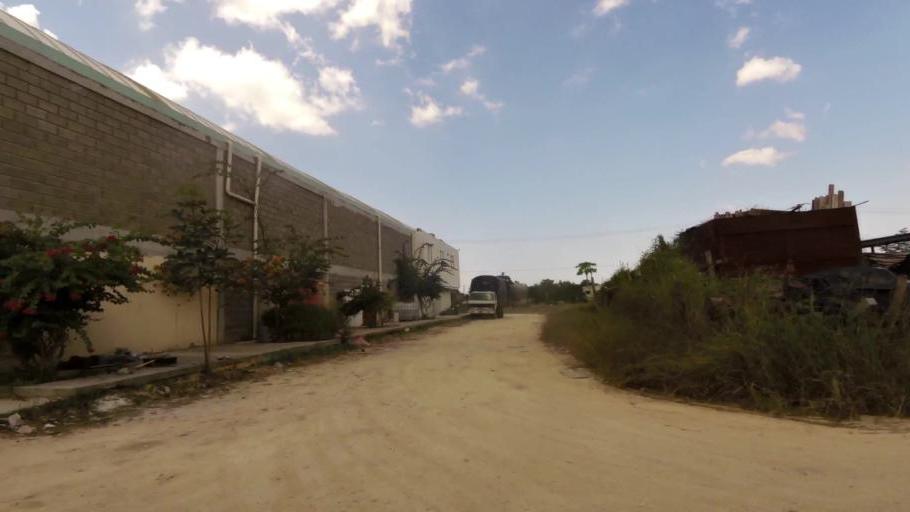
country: CO
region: Bolivar
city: Cartagena
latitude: 10.3712
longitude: -75.4591
